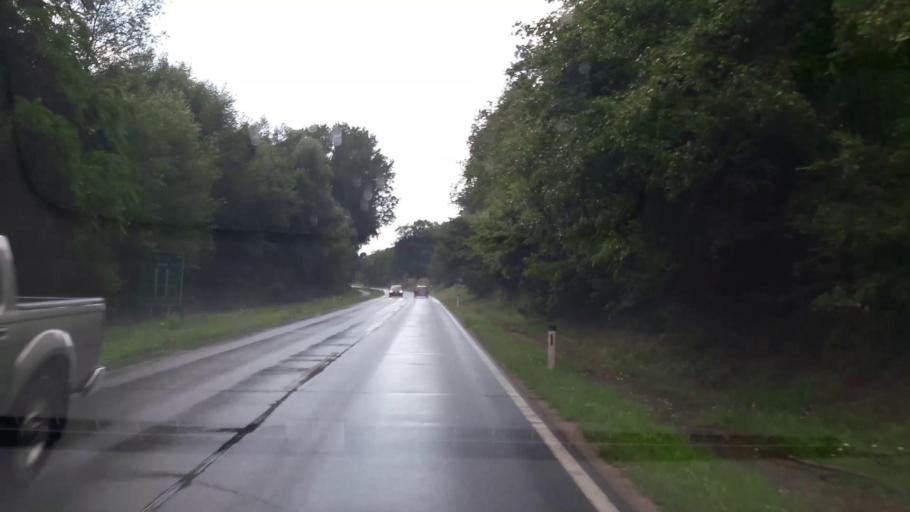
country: AT
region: Lower Austria
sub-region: Politischer Bezirk Melk
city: Emmersdorf an der Donau
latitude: 48.2481
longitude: 15.3465
